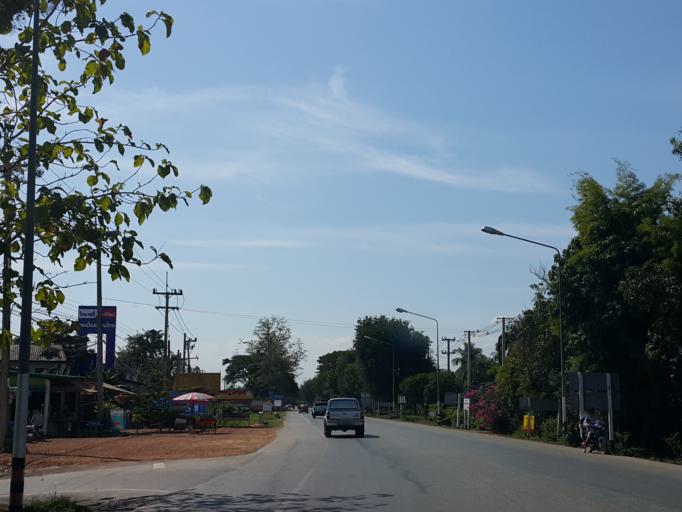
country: TH
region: Sukhothai
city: Sawankhalok
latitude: 17.2764
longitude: 99.8435
